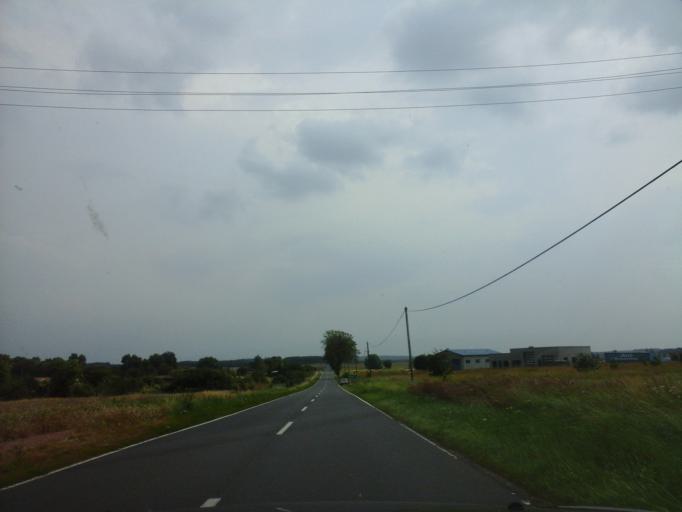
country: PL
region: Lubusz
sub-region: Powiat strzelecko-drezdenecki
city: Dobiegniew
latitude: 52.9598
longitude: 15.7509
